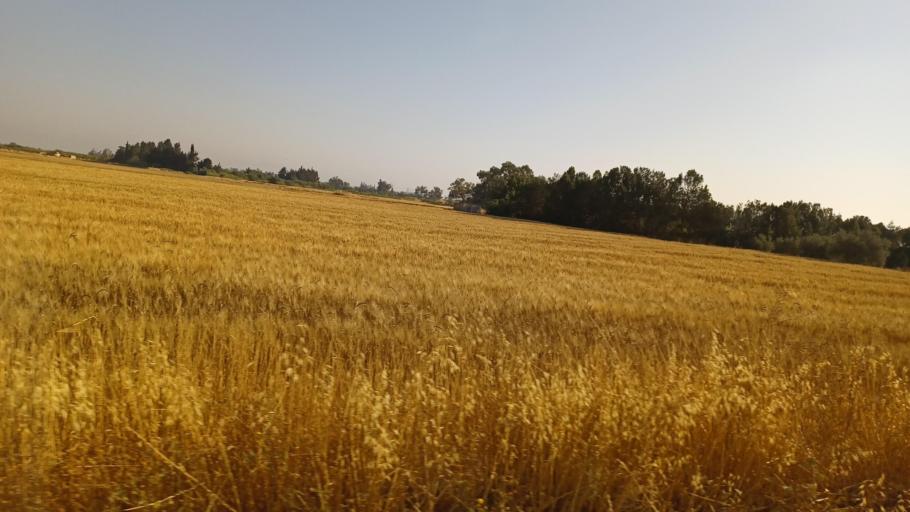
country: CY
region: Ammochostos
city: Frenaros
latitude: 35.0813
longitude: 33.9097
